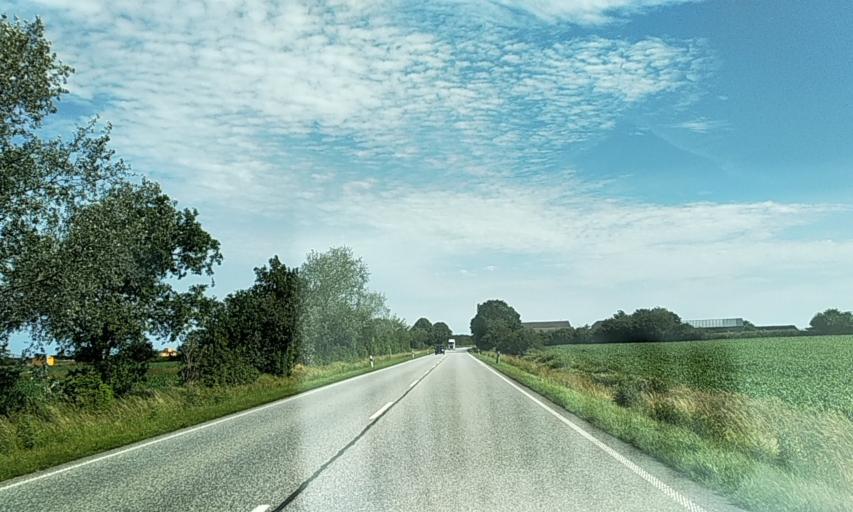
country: DE
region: Schleswig-Holstein
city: Jagel
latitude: 54.4361
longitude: 9.5333
